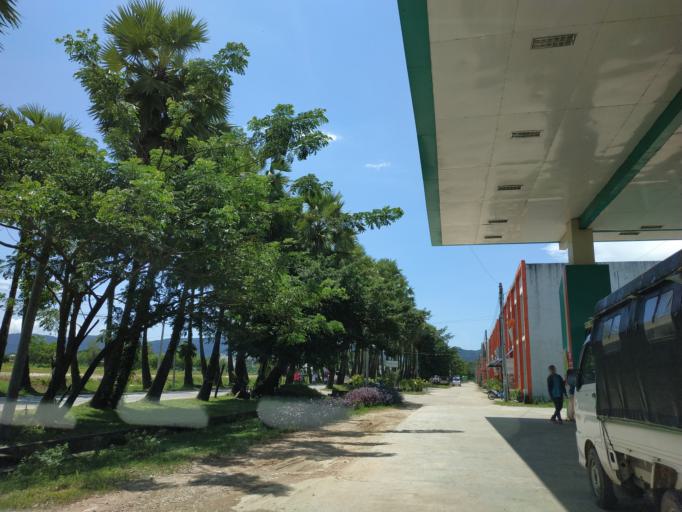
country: MM
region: Tanintharyi
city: Dawei
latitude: 14.0941
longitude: 98.1799
